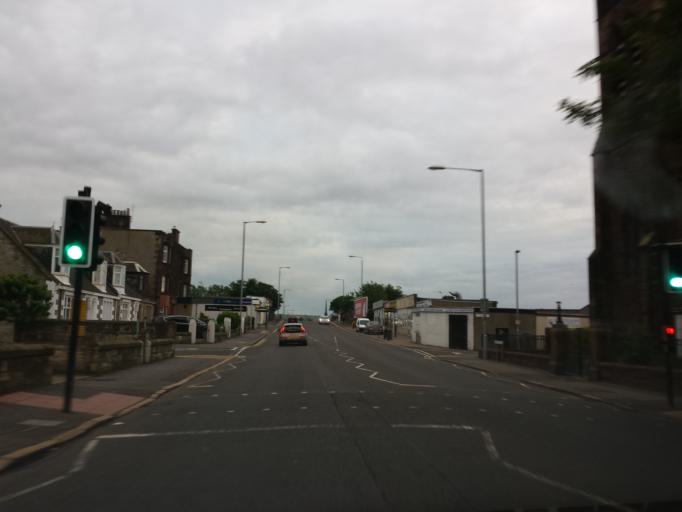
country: GB
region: Scotland
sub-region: South Ayrshire
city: Prestwick
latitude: 55.4741
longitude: -4.6244
